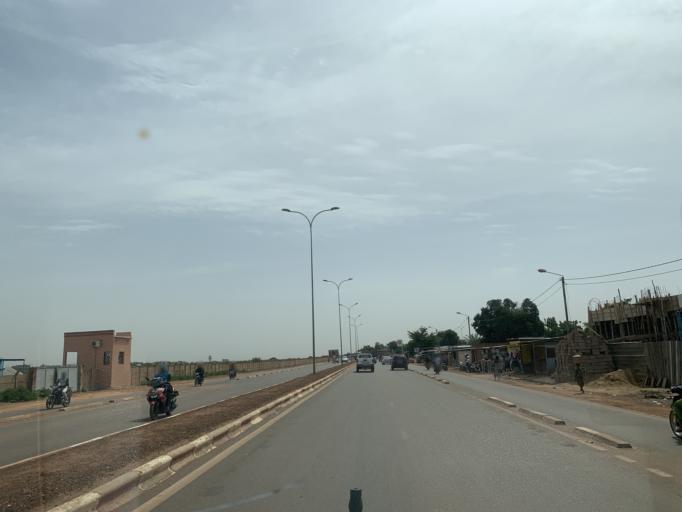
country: BF
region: Centre
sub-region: Kadiogo Province
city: Ouagadougou
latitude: 12.3379
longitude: -1.5187
